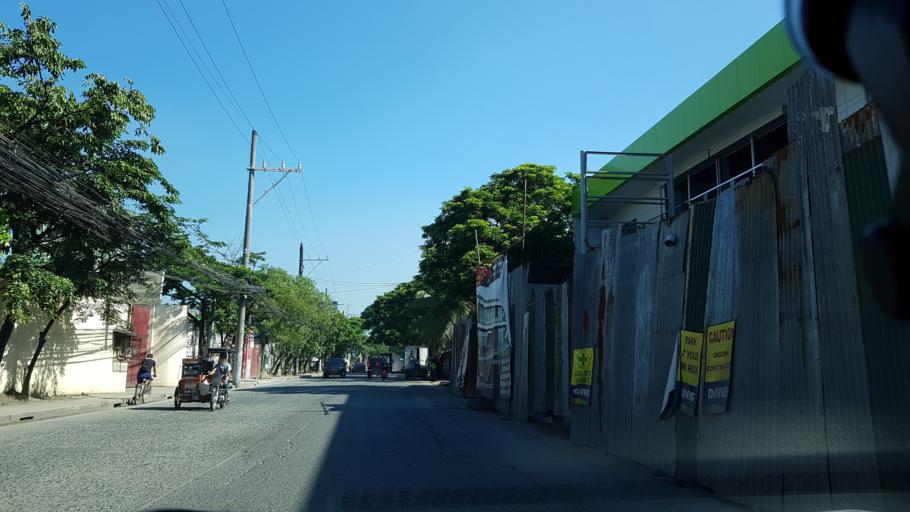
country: PH
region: Calabarzon
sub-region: Province of Rizal
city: Cainta
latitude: 14.5636
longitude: 121.0939
